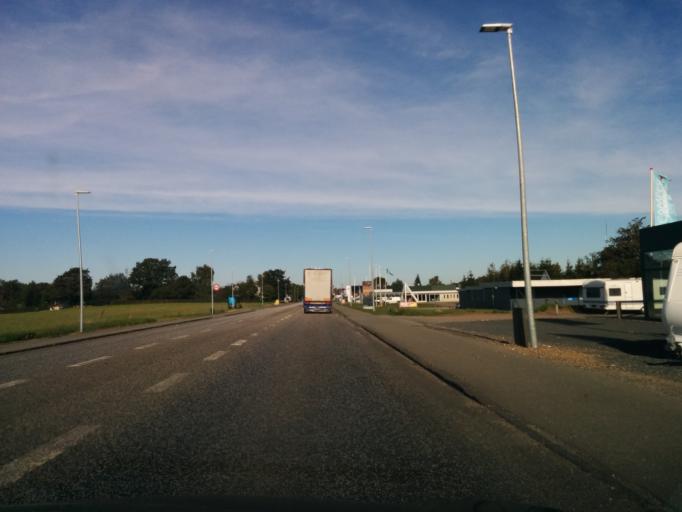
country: DK
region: South Denmark
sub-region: Kolding Kommune
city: Kolding
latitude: 55.4626
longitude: 9.4729
